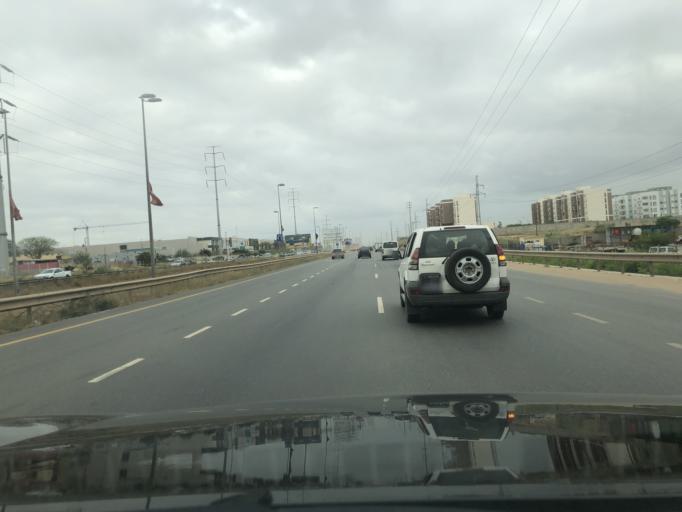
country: AO
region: Luanda
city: Luanda
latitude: -8.9739
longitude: 13.2219
